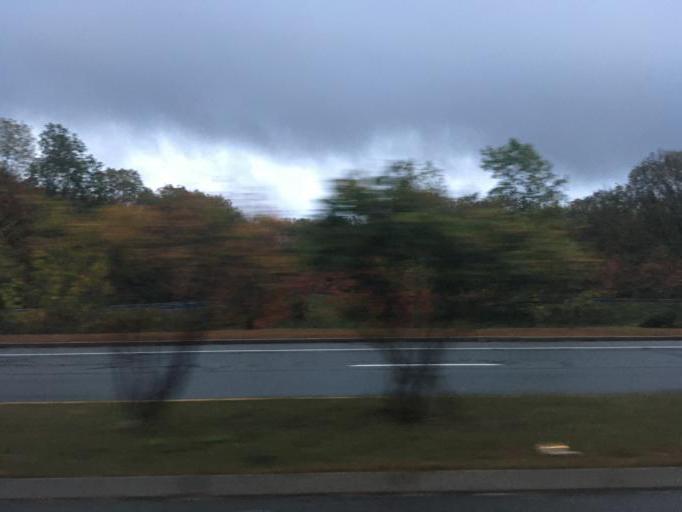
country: US
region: Rhode Island
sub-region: Kent County
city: West Warwick
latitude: 41.6959
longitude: -71.4980
